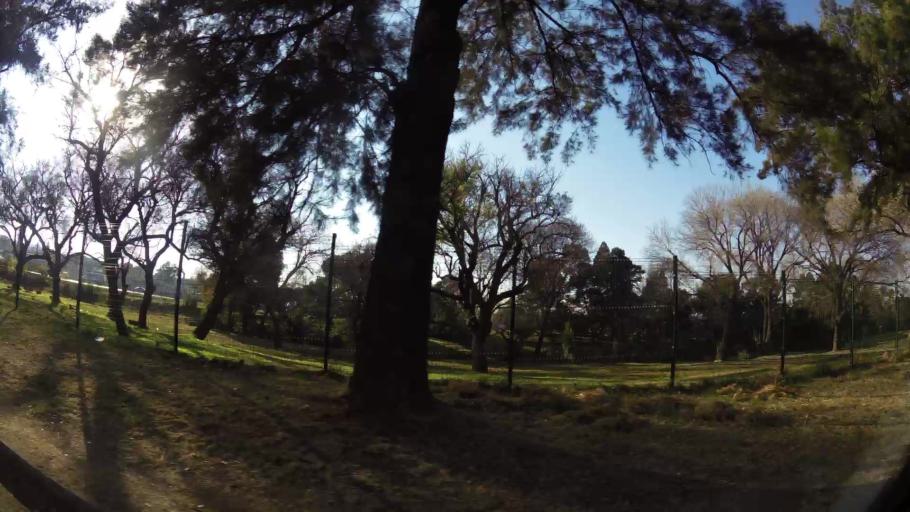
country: ZA
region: Gauteng
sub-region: Ekurhuleni Metropolitan Municipality
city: Germiston
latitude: -26.2009
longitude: 28.1325
